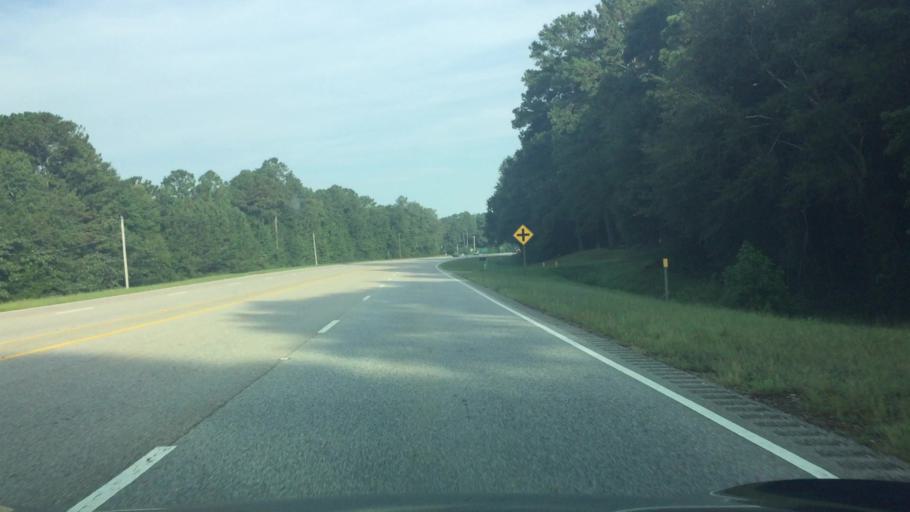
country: US
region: Alabama
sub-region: Covington County
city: Andalusia
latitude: 31.4052
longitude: -86.5980
